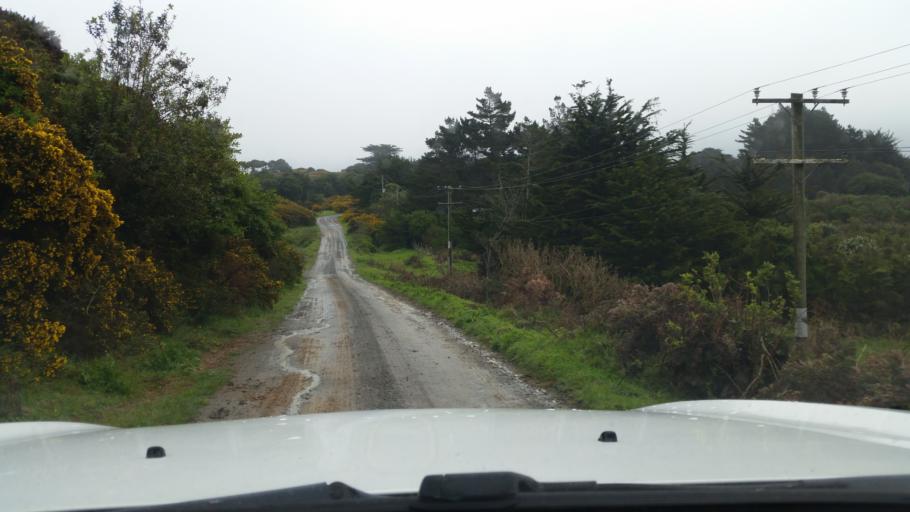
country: NZ
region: Chatham Islands
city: Waitangi
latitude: -43.9677
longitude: -176.5474
